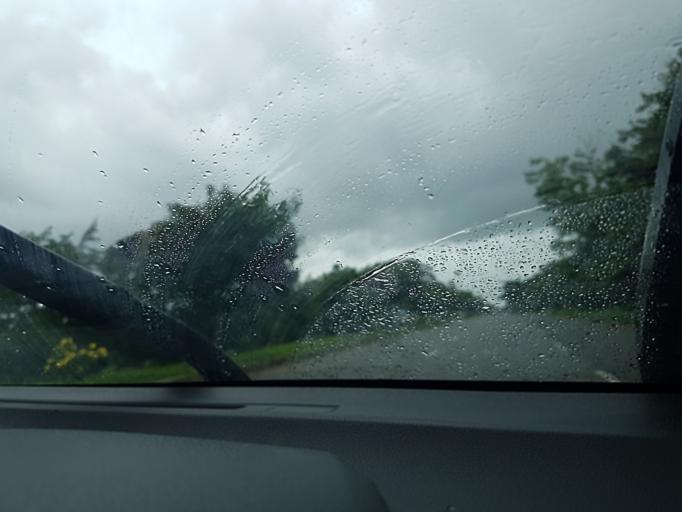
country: MM
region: Bago
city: Thanatpin
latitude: 17.1248
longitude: 96.2669
